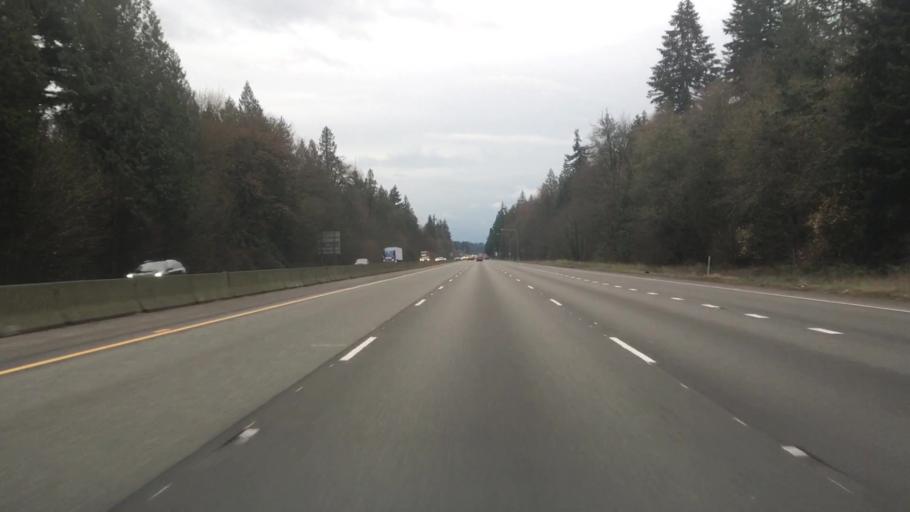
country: US
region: Washington
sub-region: Thurston County
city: Tumwater
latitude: 46.9483
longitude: -122.9389
